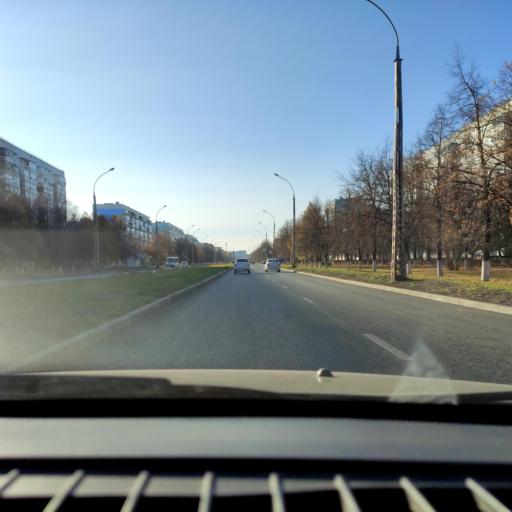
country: RU
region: Samara
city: Tol'yatti
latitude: 53.5398
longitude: 49.3300
